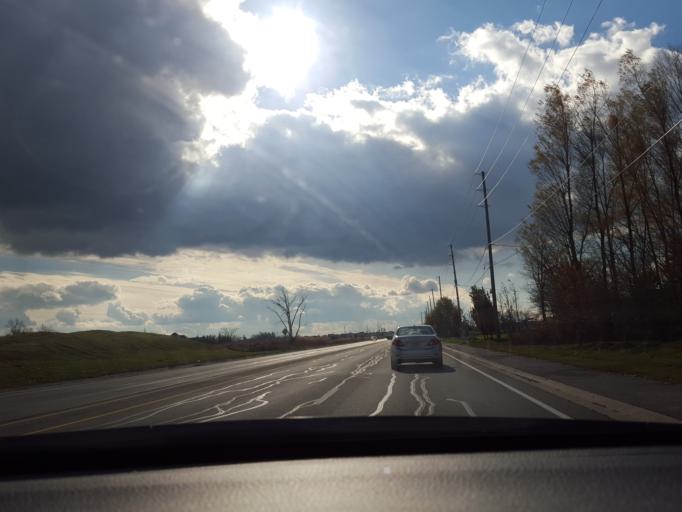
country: CA
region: Ontario
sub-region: Halton
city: Milton
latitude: 43.5390
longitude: -79.8260
